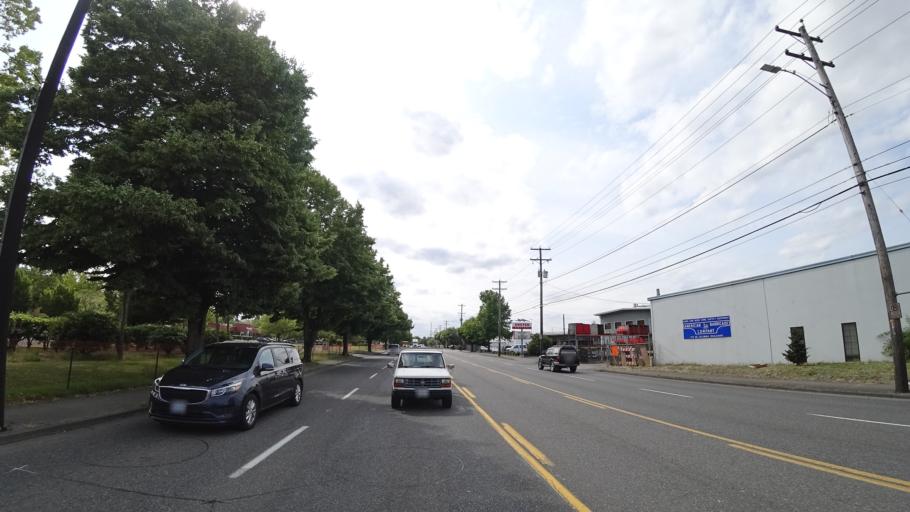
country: US
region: Washington
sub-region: Clark County
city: Vancouver
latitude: 45.5818
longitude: -122.6637
